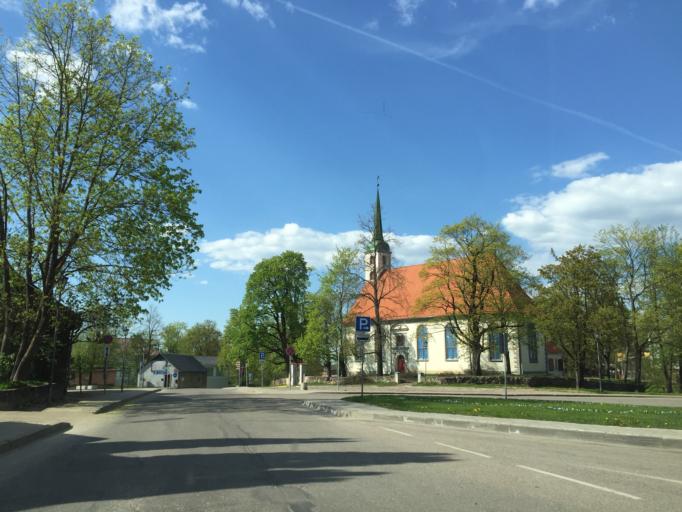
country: LV
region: Limbazu Rajons
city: Limbazi
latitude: 57.5142
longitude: 24.7158
